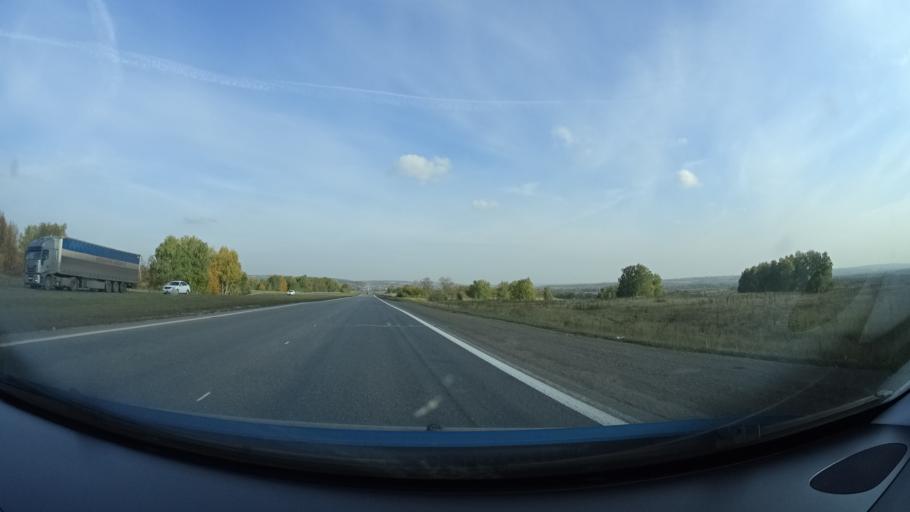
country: RU
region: Bashkortostan
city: Chishmy
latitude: 54.6516
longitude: 55.5097
